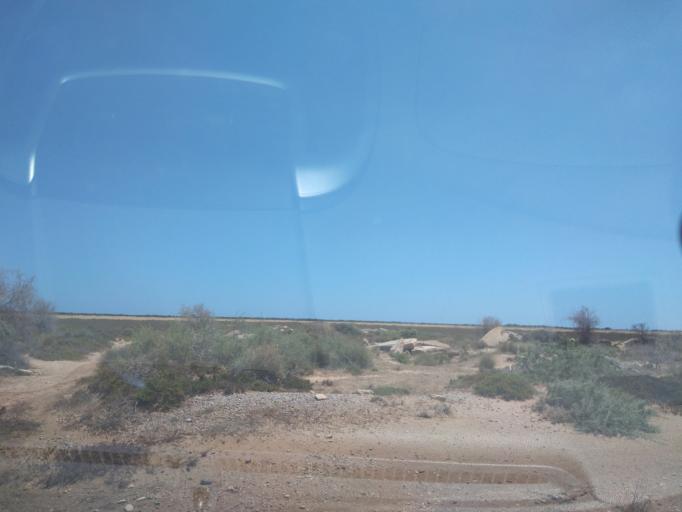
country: TN
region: Susah
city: Harqalah
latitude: 36.1692
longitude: 10.4499
